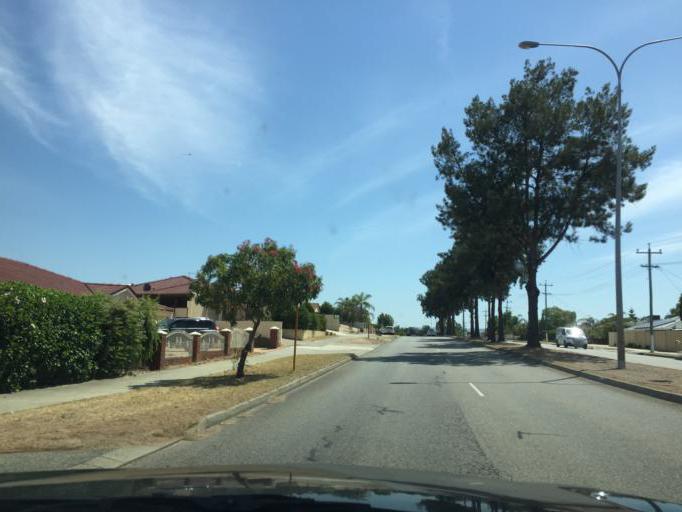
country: AU
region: Western Australia
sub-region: Gosnells
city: Thornlie
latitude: -32.0731
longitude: 115.9637
